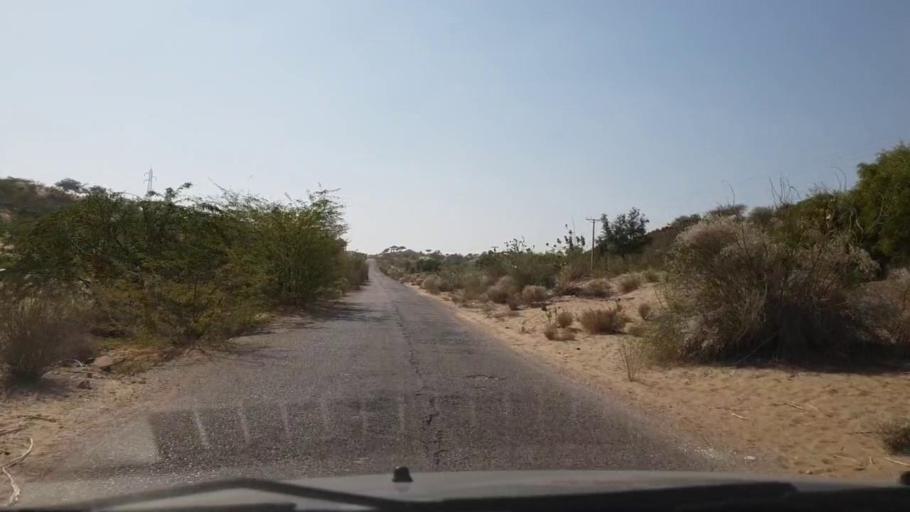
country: PK
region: Sindh
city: Diplo
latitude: 24.5451
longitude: 69.6493
